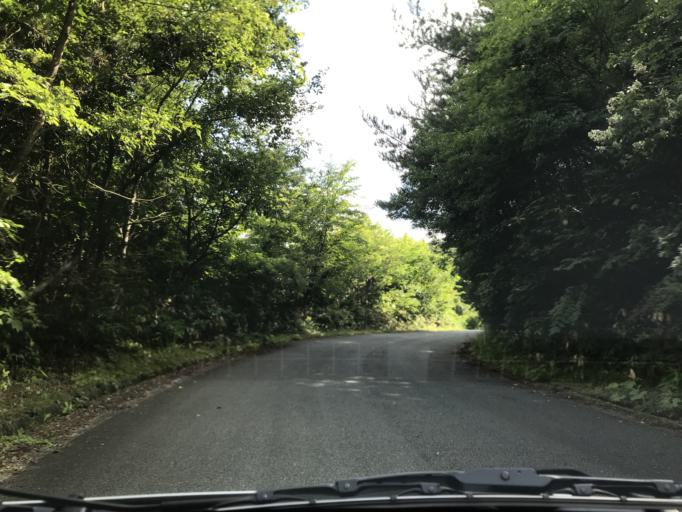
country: JP
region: Iwate
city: Mizusawa
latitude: 39.0265
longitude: 141.1894
